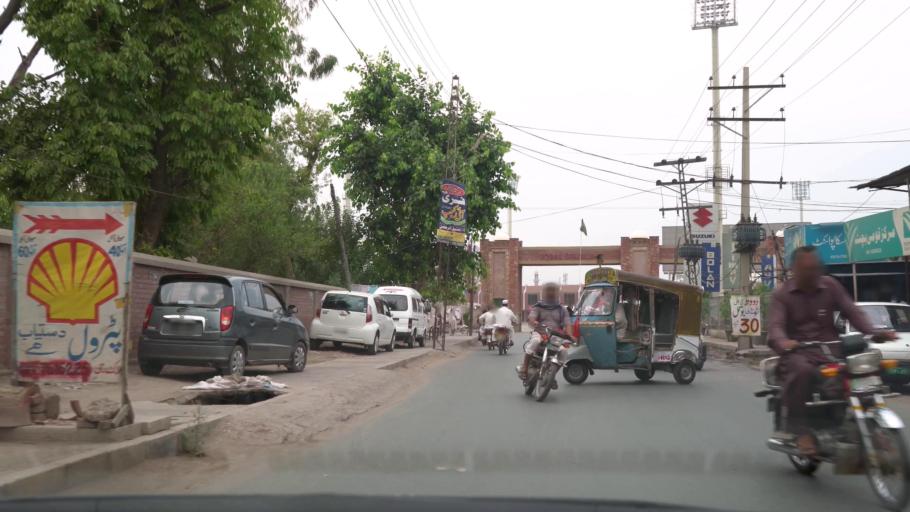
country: PK
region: Punjab
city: Faisalabad
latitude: 31.4332
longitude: 73.0857
